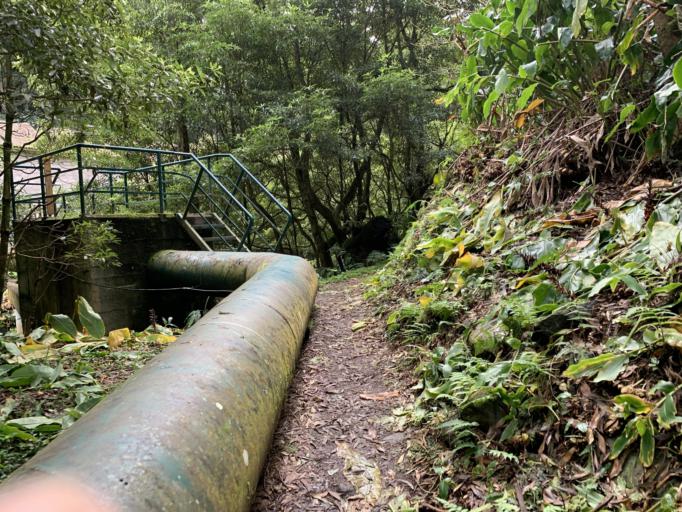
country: PT
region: Azores
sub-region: Ribeira Grande
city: Rabo de Peixe
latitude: 37.7955
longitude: -25.4925
